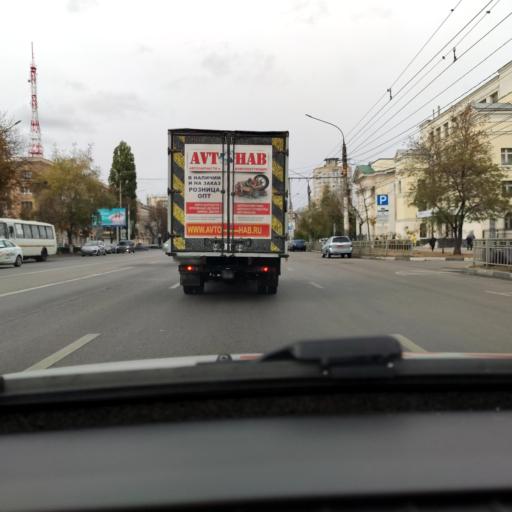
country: RU
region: Voronezj
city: Voronezh
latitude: 51.6513
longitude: 39.1920
